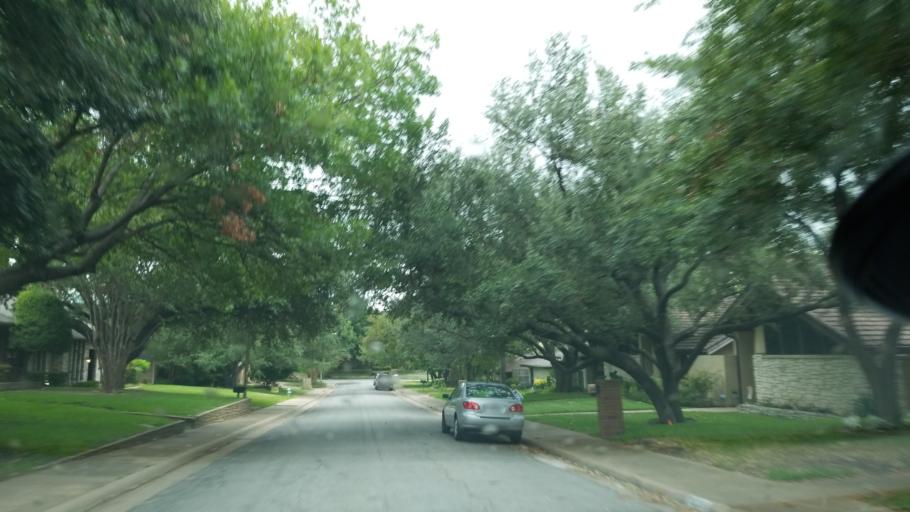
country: US
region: Texas
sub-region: Dallas County
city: Richardson
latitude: 32.8960
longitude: -96.7377
